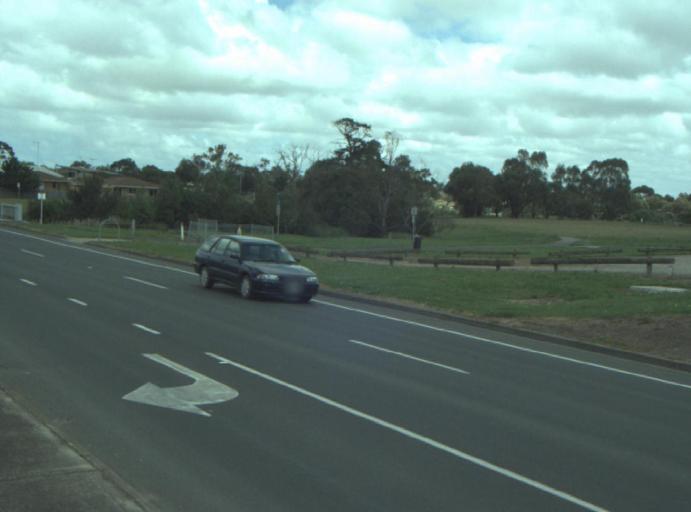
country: AU
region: Victoria
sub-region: Greater Geelong
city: Breakwater
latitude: -38.1899
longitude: 144.3434
